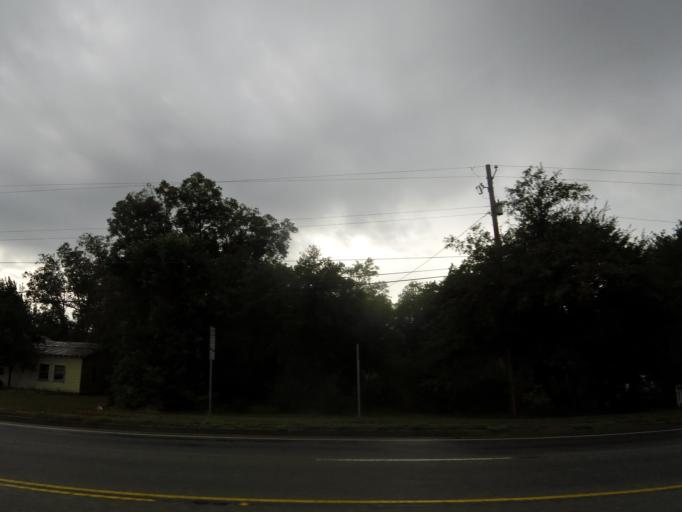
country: US
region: Georgia
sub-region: Wayne County
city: Jesup
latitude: 31.5937
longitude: -81.8689
